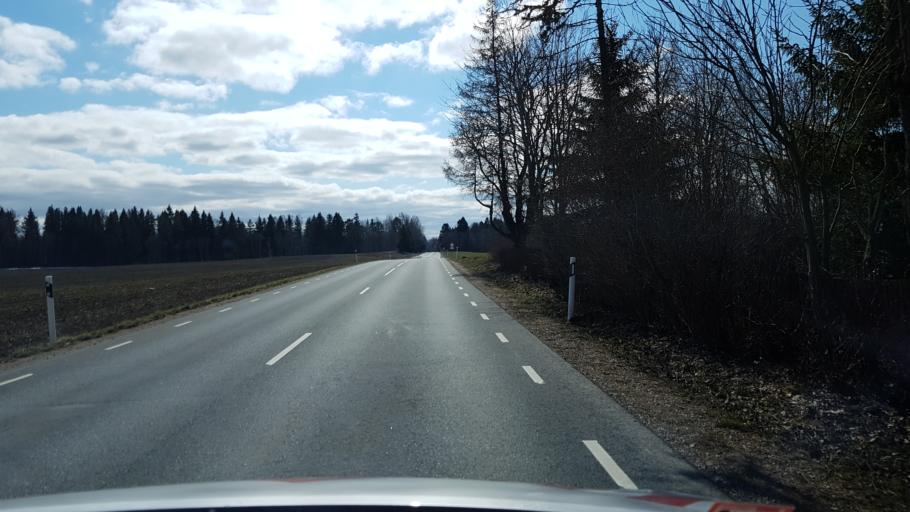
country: EE
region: Laeaene-Virumaa
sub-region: Tapa vald
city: Tapa
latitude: 59.3636
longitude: 26.0009
